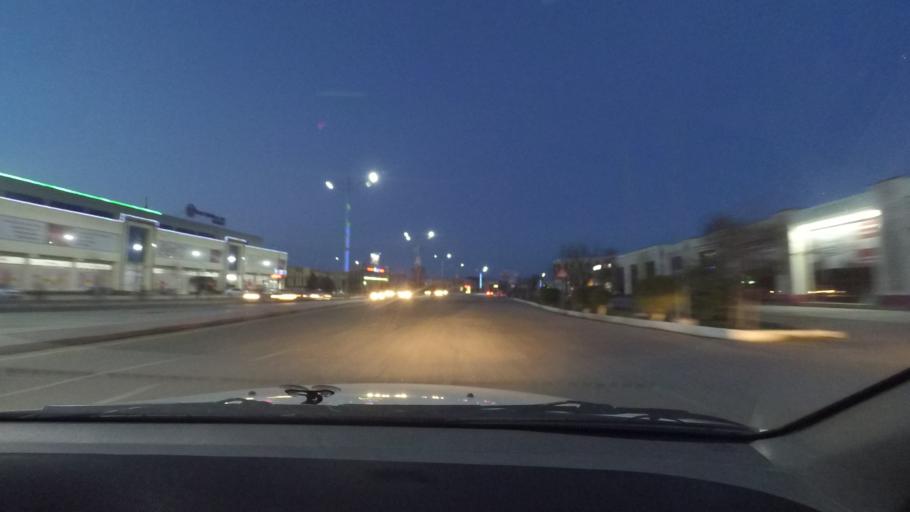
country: UZ
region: Bukhara
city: Bukhara
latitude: 39.7823
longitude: 64.4127
